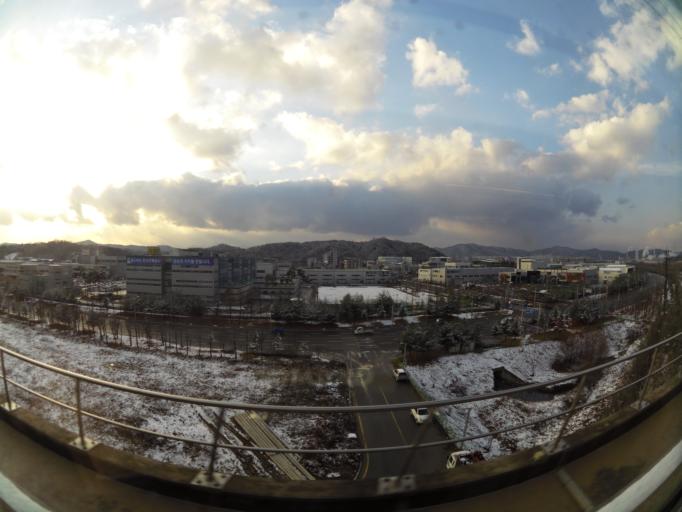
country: KR
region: Daejeon
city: Songgang-dong
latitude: 36.4159
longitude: 127.4157
